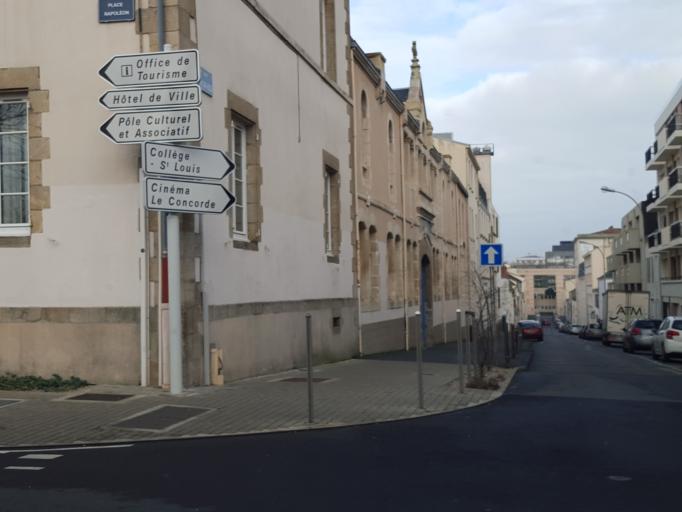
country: FR
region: Pays de la Loire
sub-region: Departement de la Vendee
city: La Roche-sur-Yon
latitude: 46.6714
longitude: -1.4258
